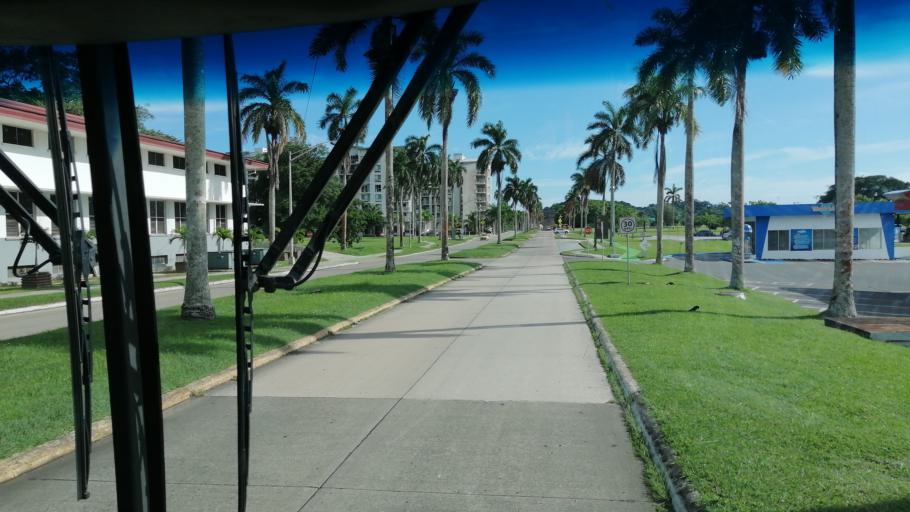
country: PA
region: Panama
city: Veracruz
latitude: 8.9189
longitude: -79.5920
